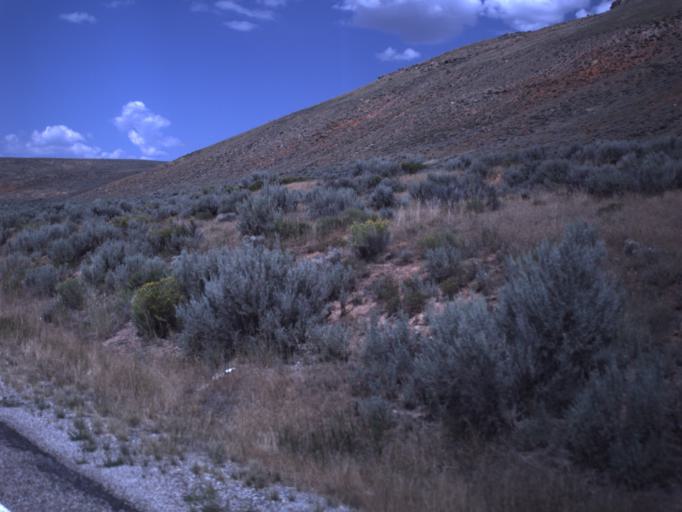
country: US
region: Utah
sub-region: Rich County
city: Randolph
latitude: 41.7691
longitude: -111.1724
